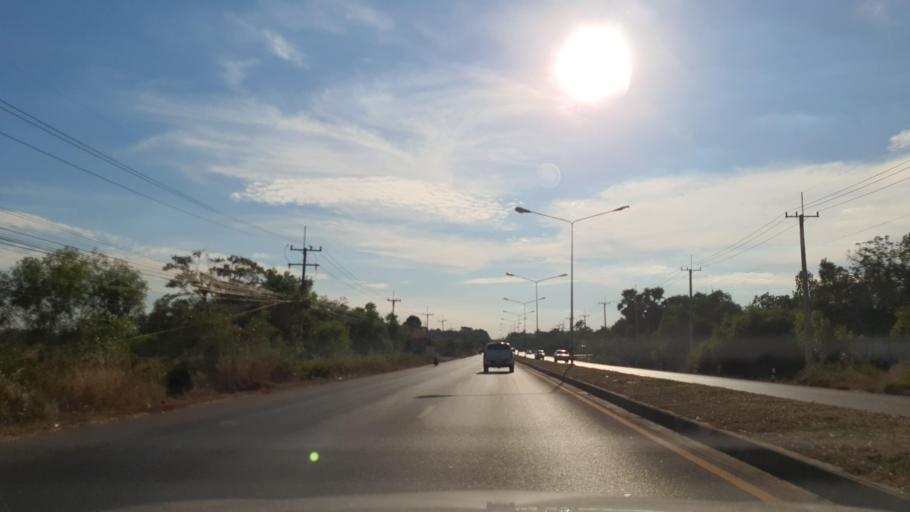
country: TH
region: Maha Sarakham
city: Kantharawichai
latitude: 16.3398
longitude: 103.3136
